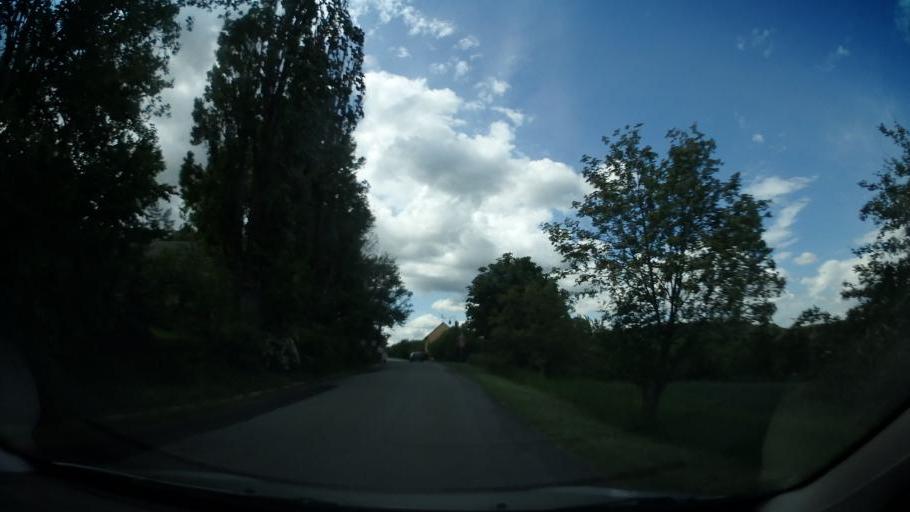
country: CZ
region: South Moravian
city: Velke Opatovice
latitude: 49.6239
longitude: 16.6061
